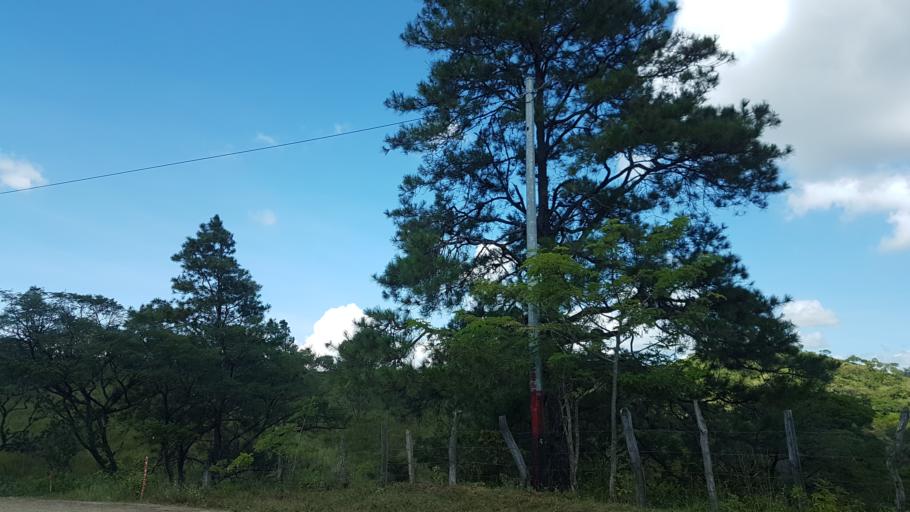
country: HN
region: El Paraiso
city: Oropoli
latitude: 13.7421
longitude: -86.7039
